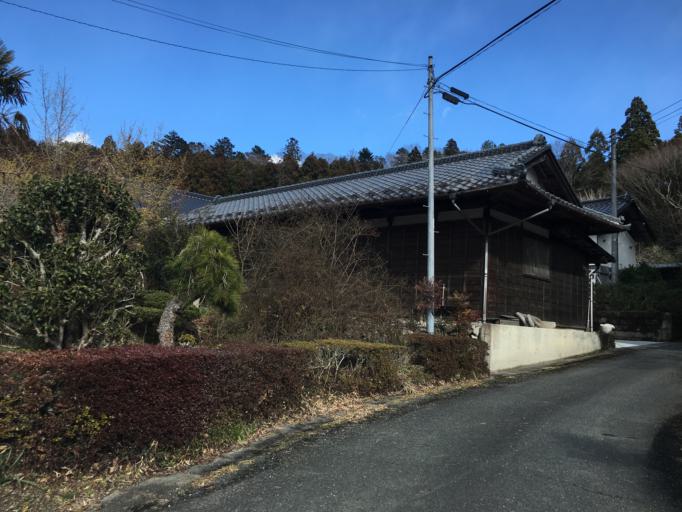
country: JP
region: Fukushima
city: Iwaki
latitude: 36.9748
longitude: 140.7656
